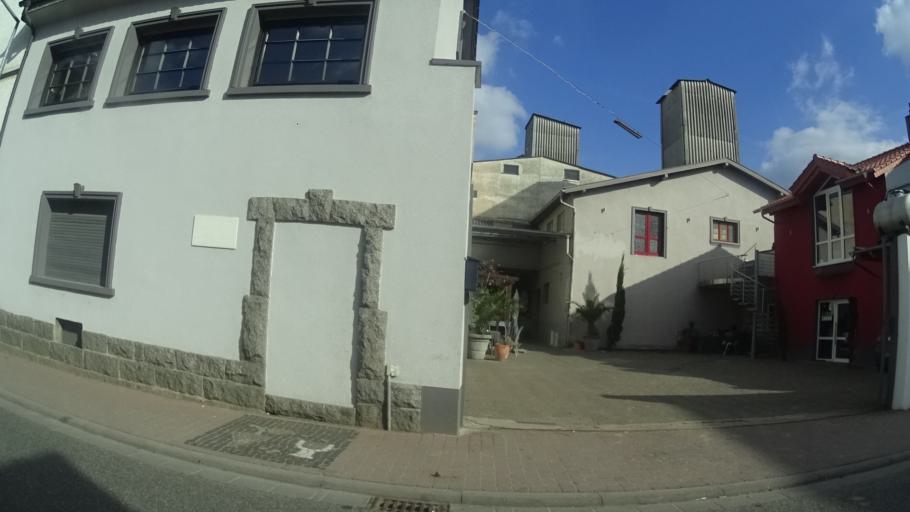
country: DE
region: Rheinland-Pfalz
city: Mettenheim
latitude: 49.7396
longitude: 8.3257
